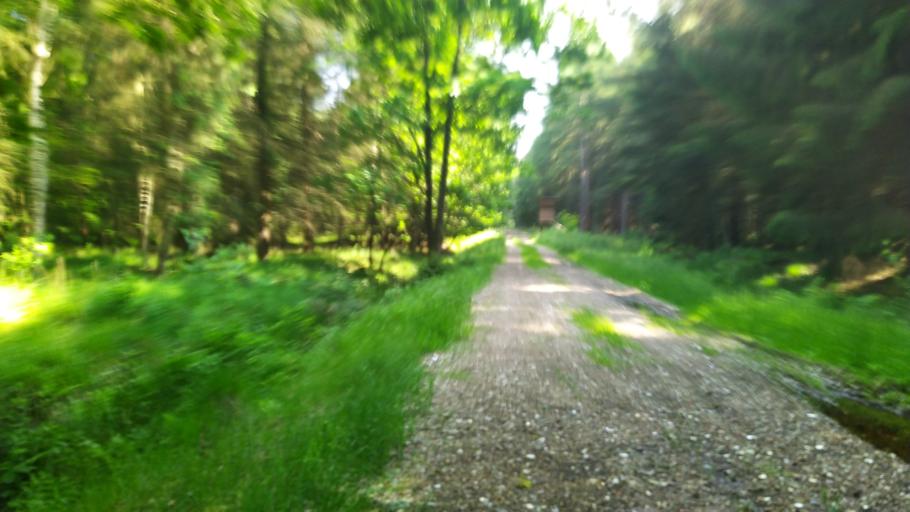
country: DE
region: Lower Saxony
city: Wohnste
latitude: 53.3940
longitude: 9.5151
